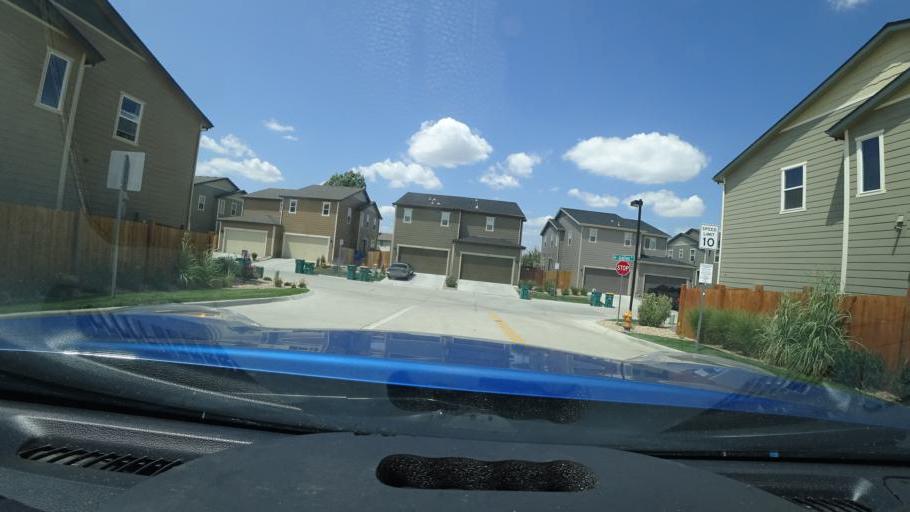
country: US
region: Colorado
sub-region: Adams County
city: Aurora
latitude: 39.6930
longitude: -104.8756
